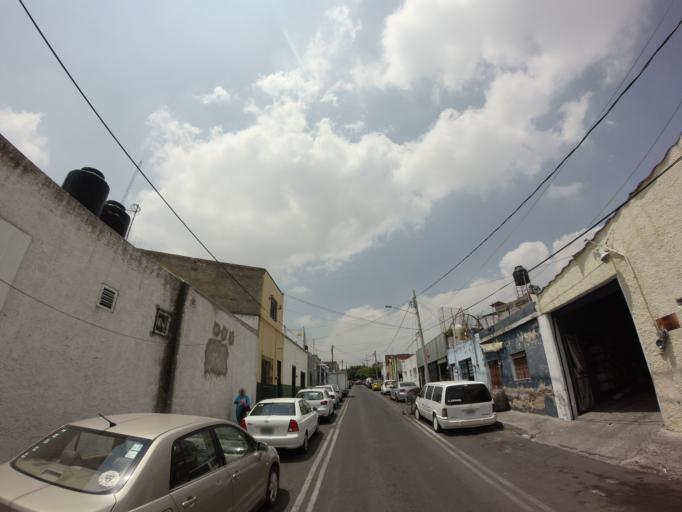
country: MX
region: Jalisco
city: Guadalajara
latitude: 20.6860
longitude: -103.3346
